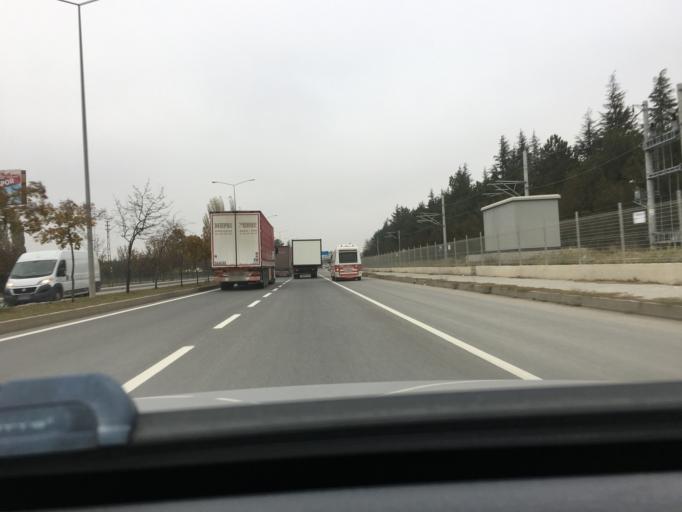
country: TR
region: Eskisehir
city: Eskisehir
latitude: 39.7646
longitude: 30.4790
